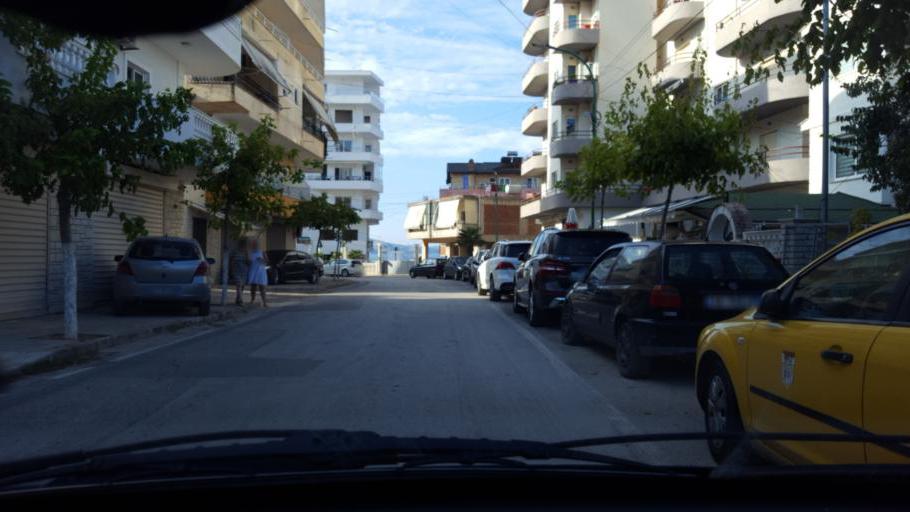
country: AL
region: Vlore
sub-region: Rrethi i Sarandes
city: Sarande
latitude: 39.8695
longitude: 19.9996
